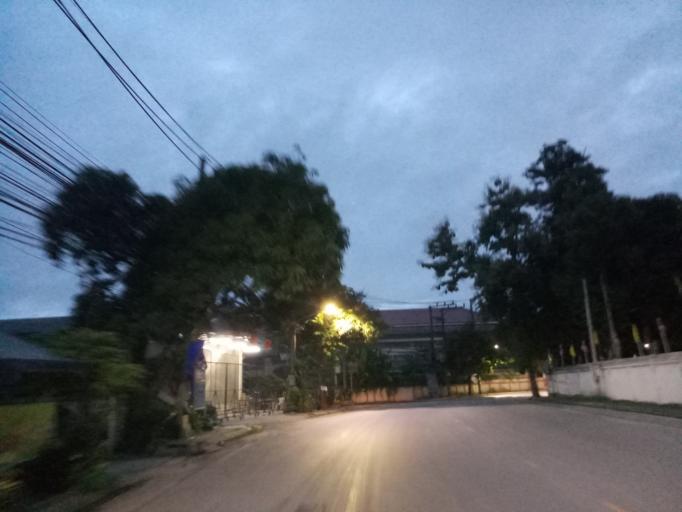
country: TH
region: Chiang Rai
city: Chiang Rai
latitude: 19.8992
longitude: 99.8258
